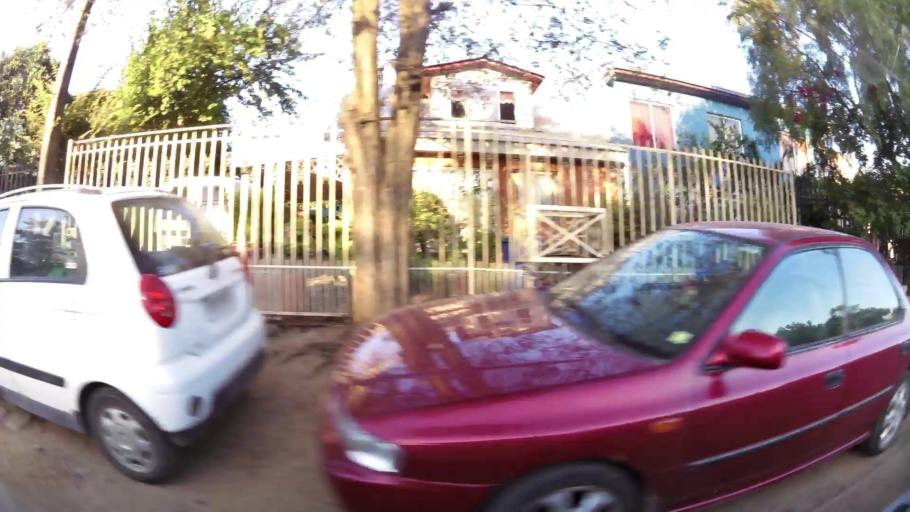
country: CL
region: Maule
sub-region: Provincia de Talca
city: Talca
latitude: -35.4419
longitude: -71.6425
